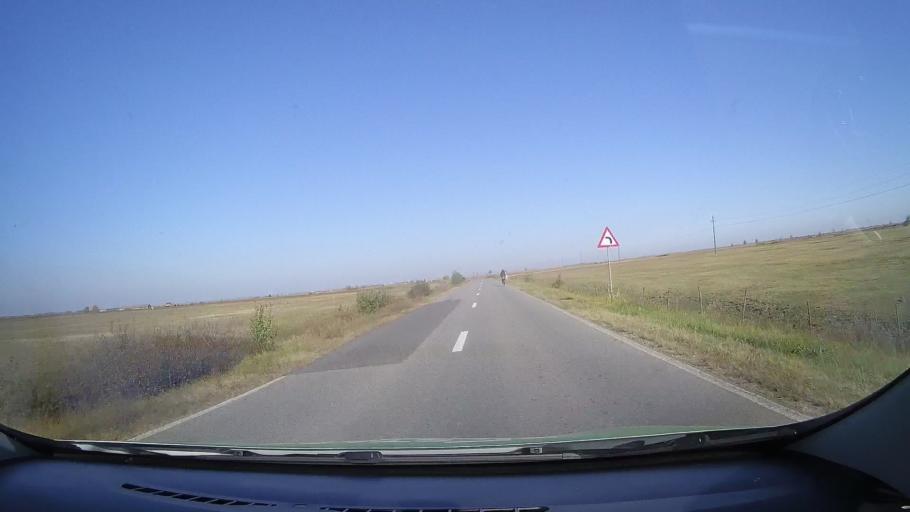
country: RO
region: Satu Mare
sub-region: Comuna Cauas
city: Cauas
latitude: 47.5441
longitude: 22.5632
